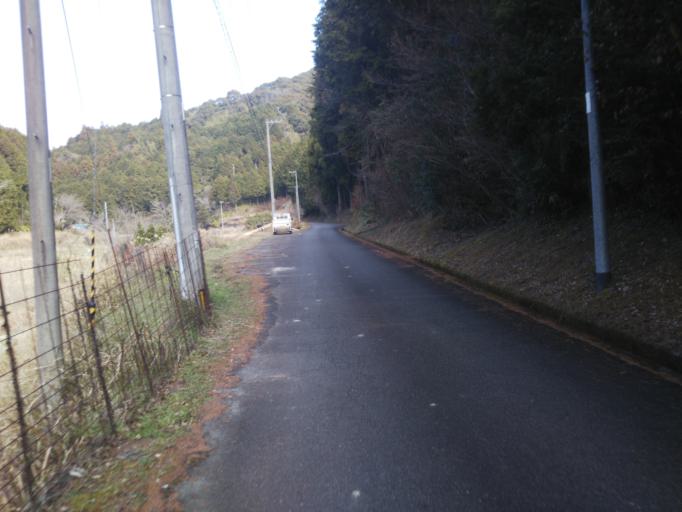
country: JP
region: Kochi
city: Nakamura
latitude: 33.0386
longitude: 132.9853
